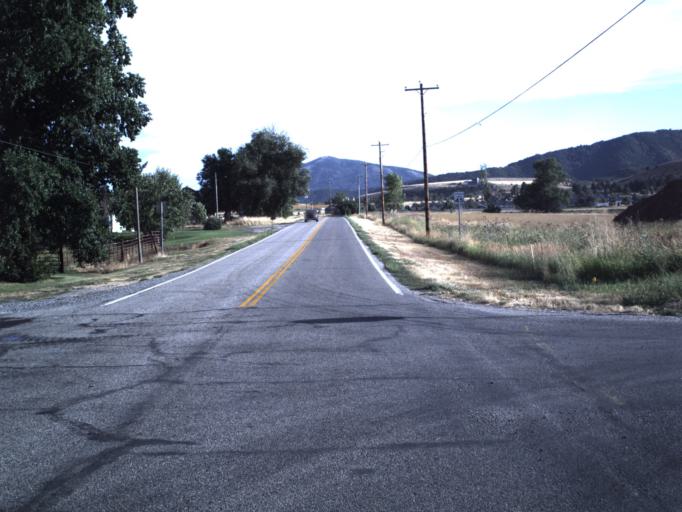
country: US
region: Utah
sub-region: Cache County
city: Wellsville
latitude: 41.6222
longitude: -111.9350
